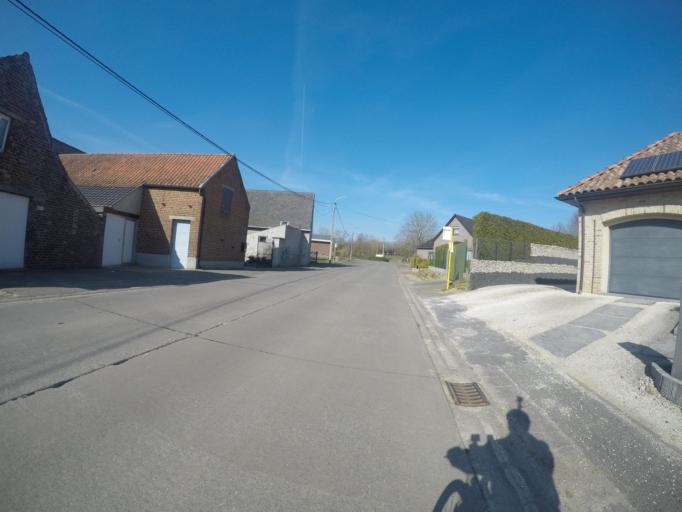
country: BE
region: Flanders
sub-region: Provincie Oost-Vlaanderen
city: Sint-Maria-Lierde
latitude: 50.8013
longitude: 3.7867
